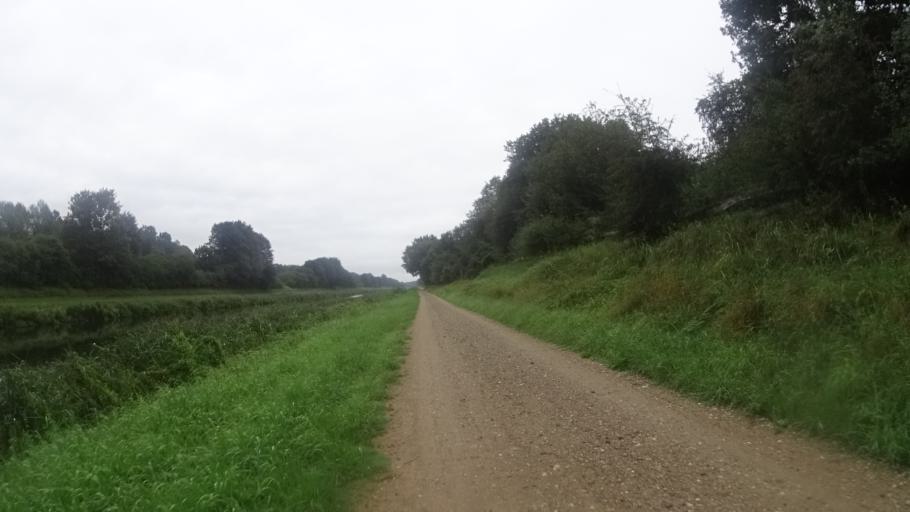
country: DE
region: Schleswig-Holstein
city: Grambek
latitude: 53.5660
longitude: 10.6771
